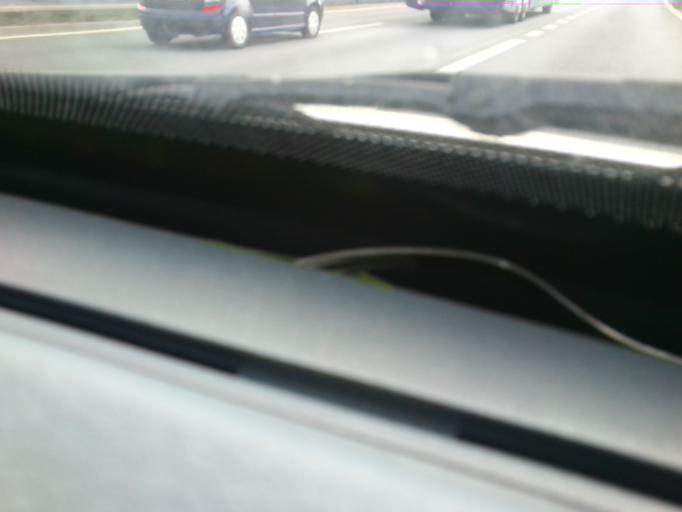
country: CZ
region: Praha
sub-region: Praha 9
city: Strizkov
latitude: 50.1397
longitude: 14.4941
